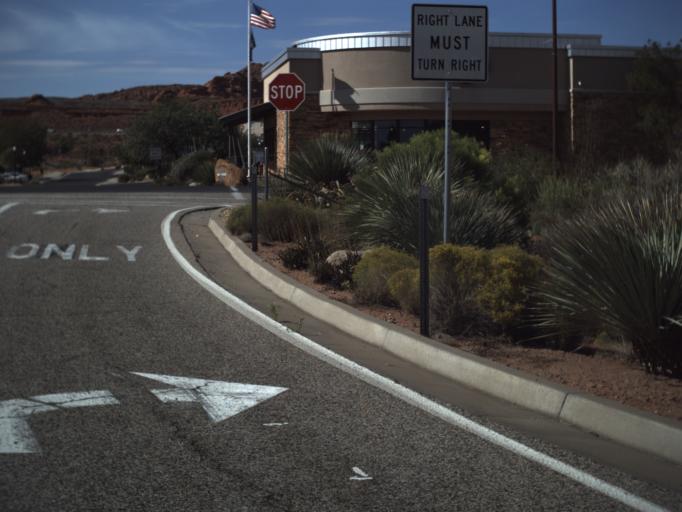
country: US
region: Utah
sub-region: Washington County
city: Washington
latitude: 37.1621
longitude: -113.4455
